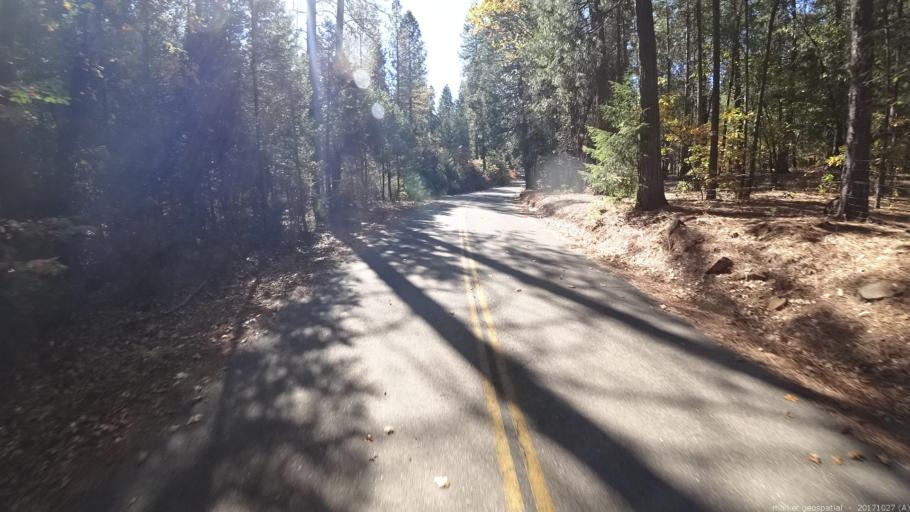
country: US
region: California
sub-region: Shasta County
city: Shingletown
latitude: 40.7389
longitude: -121.9421
